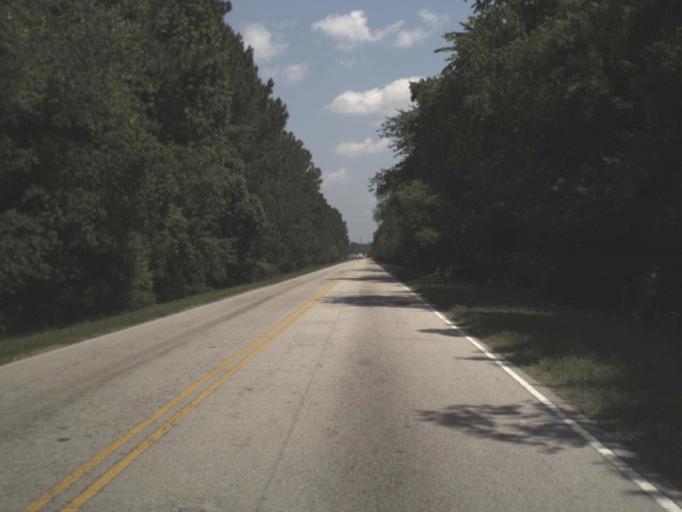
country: US
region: Florida
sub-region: Duval County
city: Jacksonville
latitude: 30.3772
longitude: -81.7649
